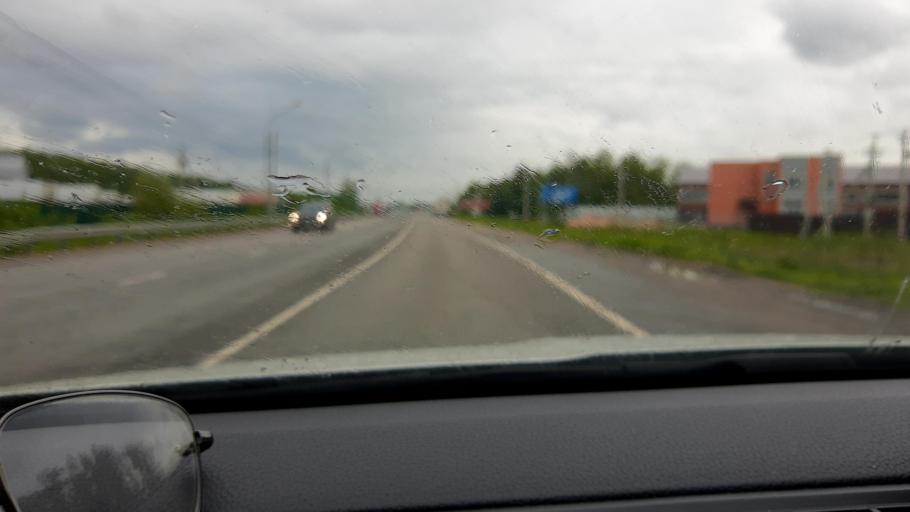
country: RU
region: Moskovskaya
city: Gorki-Leninskiye
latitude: 55.5140
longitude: 37.7869
